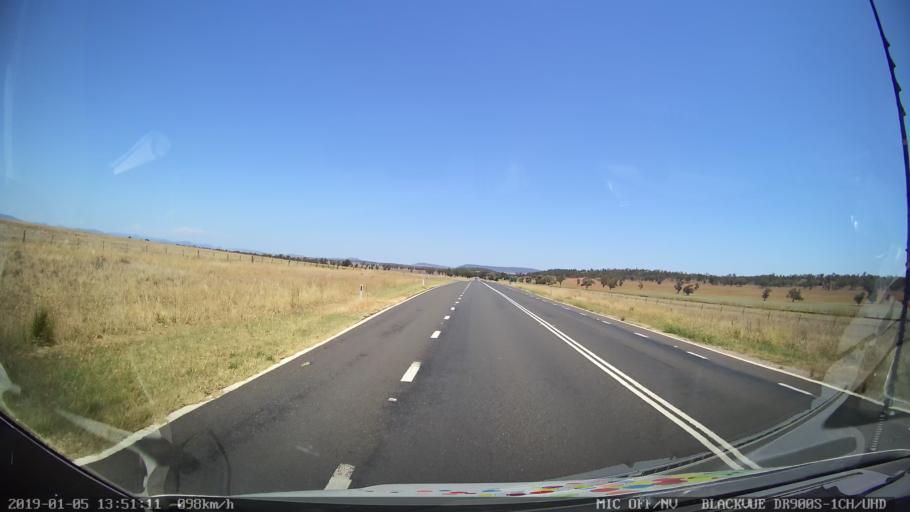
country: AU
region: New South Wales
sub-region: Gunnedah
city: Gunnedah
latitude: -31.0409
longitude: 150.2763
